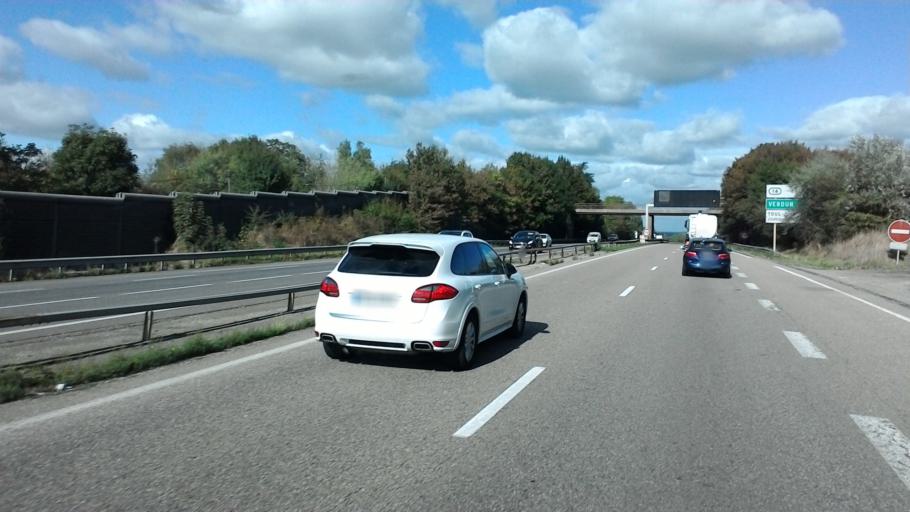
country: FR
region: Lorraine
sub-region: Departement de Meurthe-et-Moselle
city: Dommartin-les-Toul
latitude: 48.6640
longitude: 5.9131
